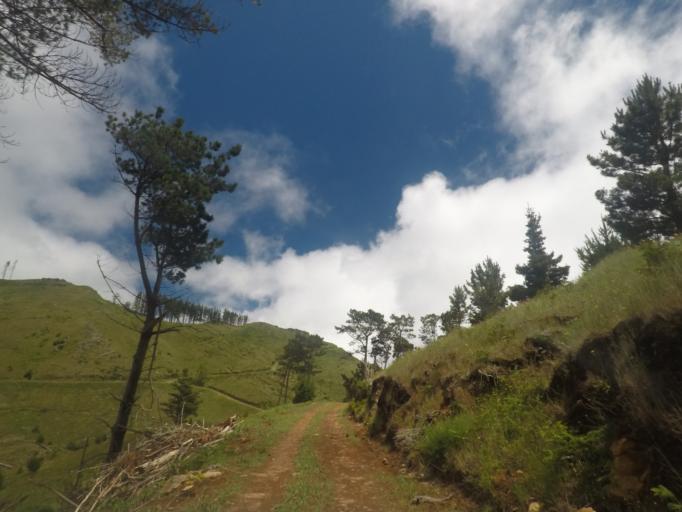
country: PT
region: Madeira
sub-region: Funchal
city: Nossa Senhora do Monte
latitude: 32.7038
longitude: -16.9047
